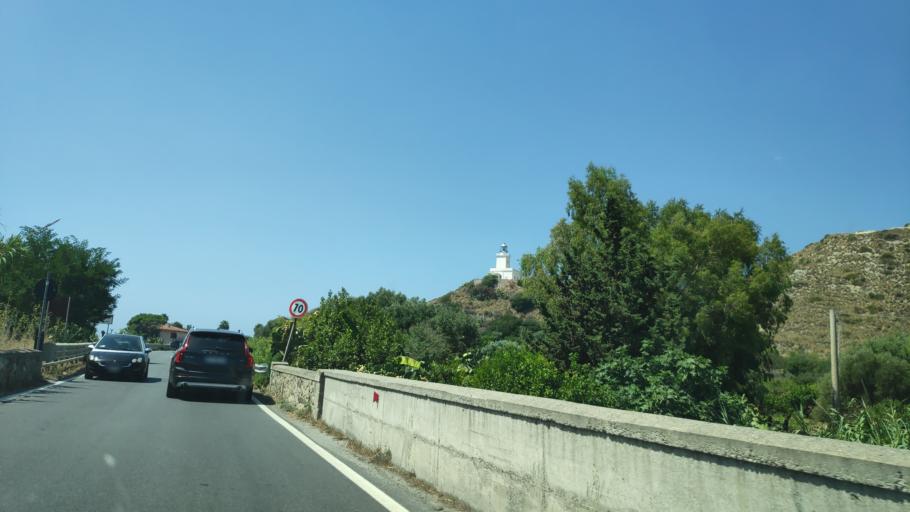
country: IT
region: Calabria
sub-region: Provincia di Reggio Calabria
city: Weather Station
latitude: 37.9269
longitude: 16.0641
